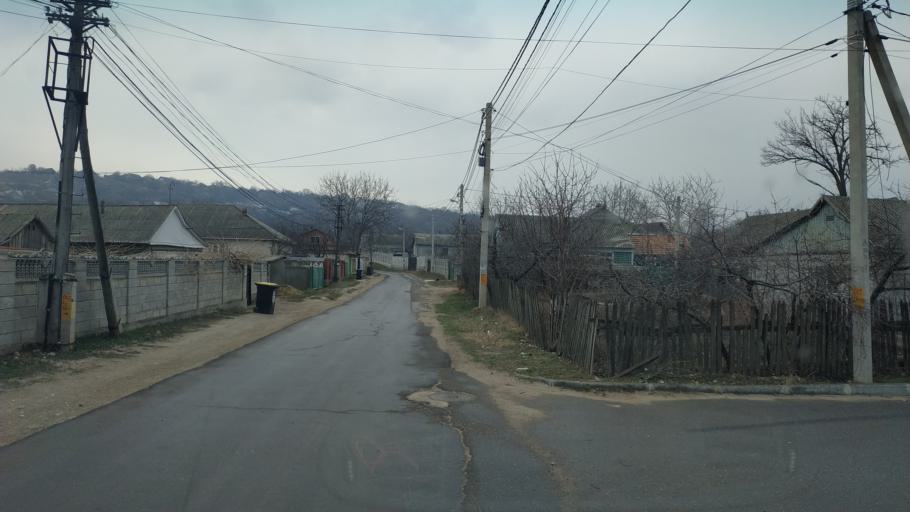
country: MD
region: Chisinau
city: Singera
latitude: 46.9128
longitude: 28.9764
